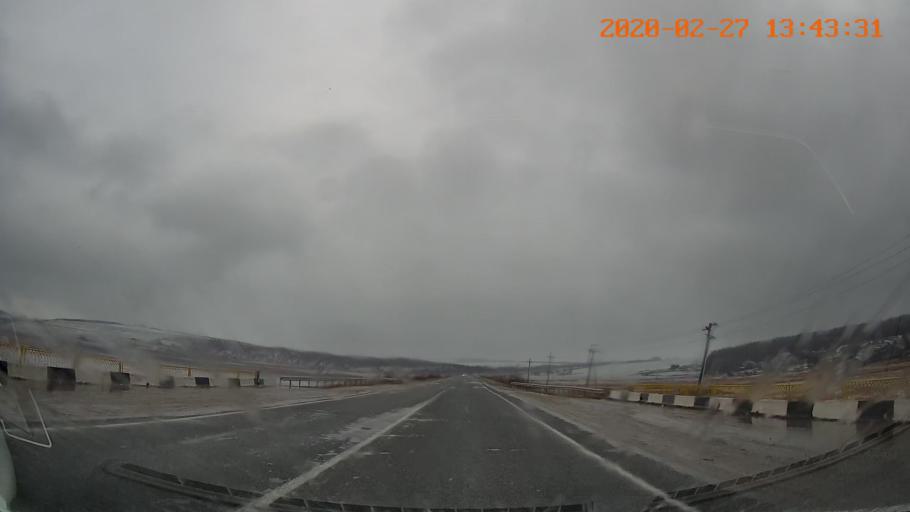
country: MD
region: Balti
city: Balti
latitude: 47.7587
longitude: 27.9644
